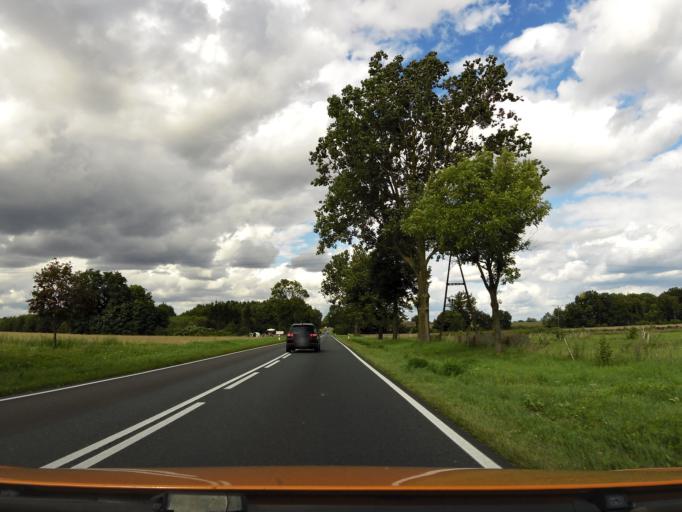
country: PL
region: West Pomeranian Voivodeship
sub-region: Powiat gryficki
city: Ploty
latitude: 53.7342
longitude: 15.2049
